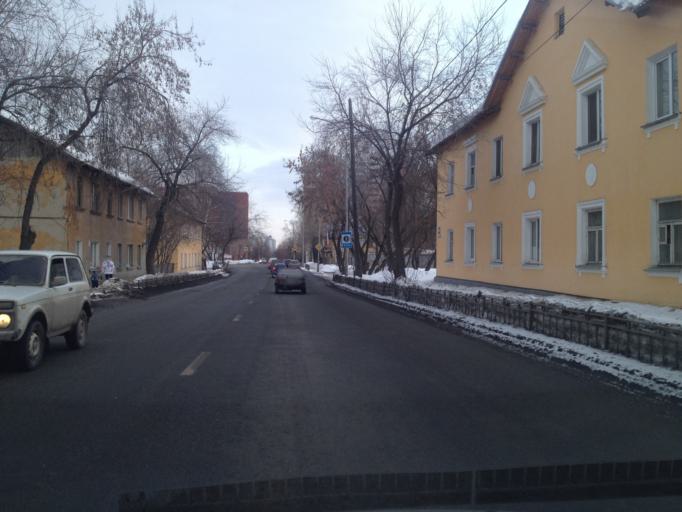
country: RU
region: Sverdlovsk
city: Yekaterinburg
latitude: 56.8642
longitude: 60.5734
